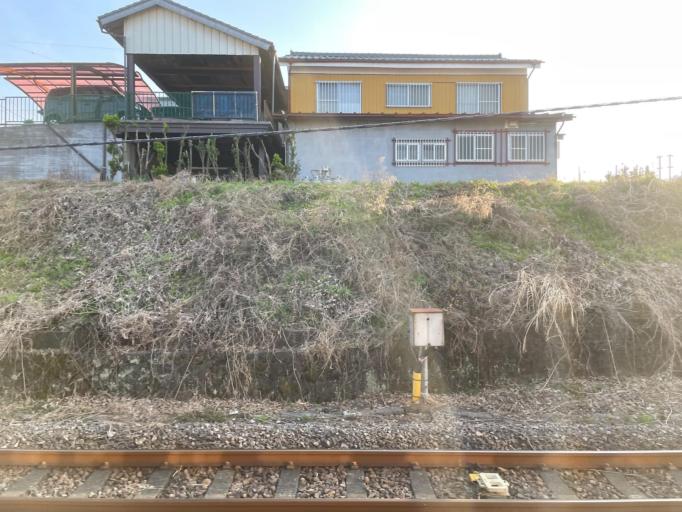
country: JP
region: Gunma
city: Annaka
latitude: 36.3099
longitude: 138.7965
